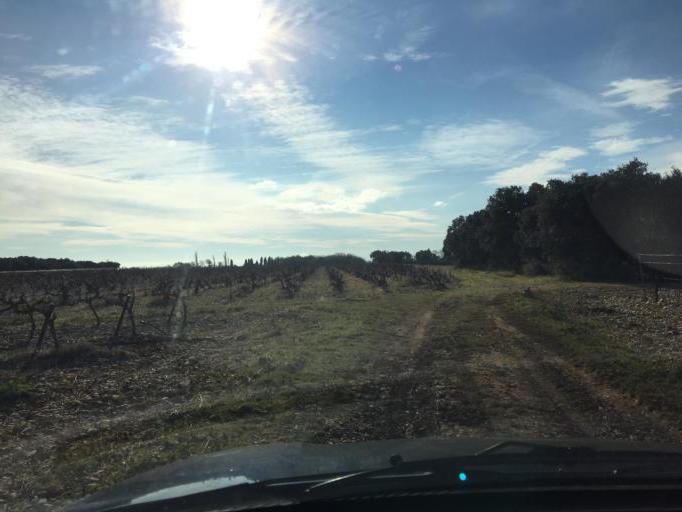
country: FR
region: Provence-Alpes-Cote d'Azur
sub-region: Departement du Vaucluse
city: Camaret-sur-Aigues
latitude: 44.1509
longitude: 4.8960
